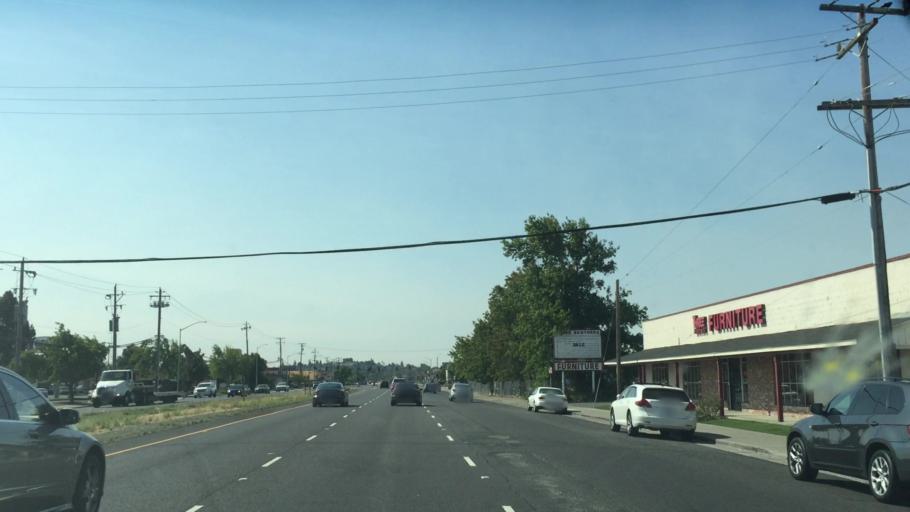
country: US
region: California
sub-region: Solano County
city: Vallejo
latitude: 38.1256
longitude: -122.2556
